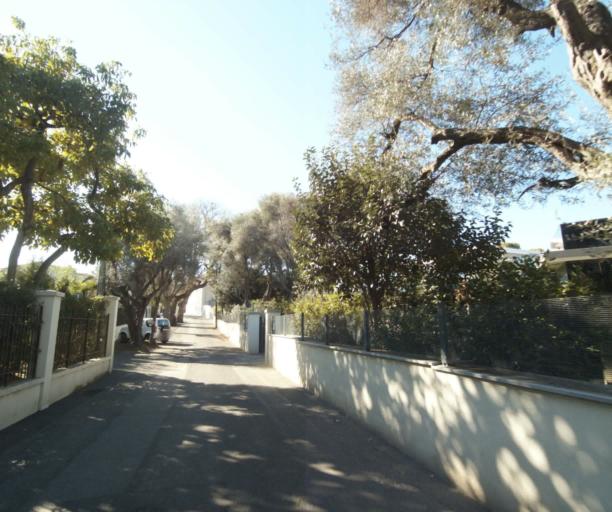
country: FR
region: Provence-Alpes-Cote d'Azur
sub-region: Departement des Alpes-Maritimes
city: Antibes
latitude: 43.5661
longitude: 7.1206
